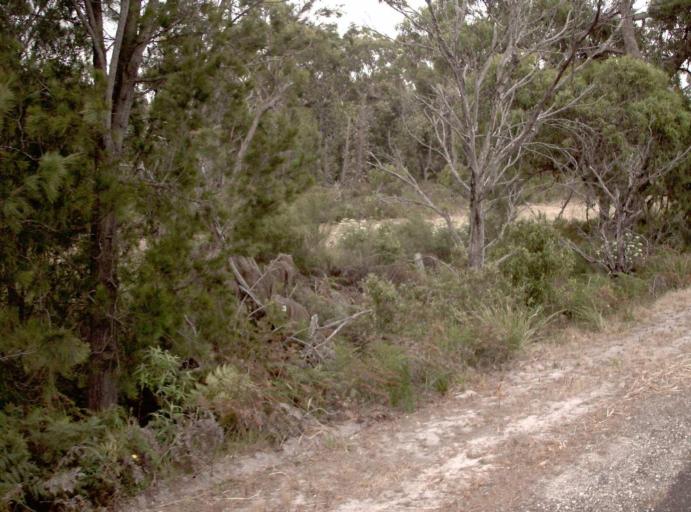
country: AU
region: Victoria
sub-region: Wellington
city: Sale
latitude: -38.1778
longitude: 147.3795
